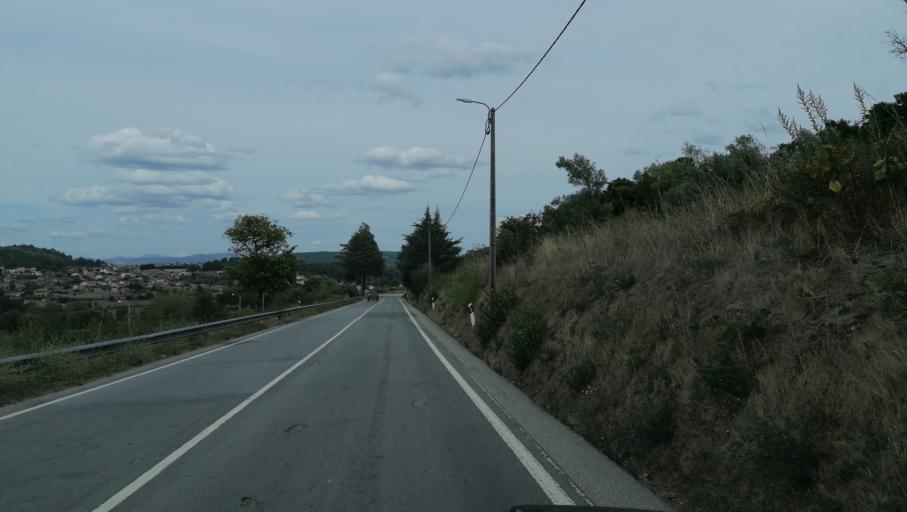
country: PT
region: Vila Real
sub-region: Vila Pouca de Aguiar
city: Vila Pouca de Aguiar
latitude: 41.5312
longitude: -7.6108
